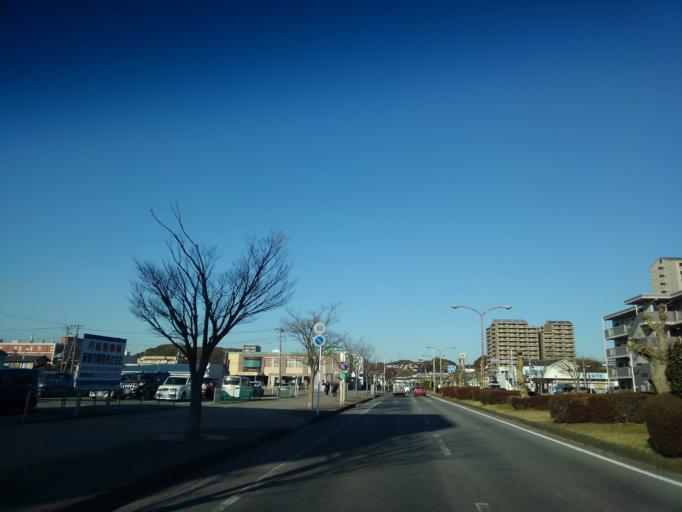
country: JP
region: Chiba
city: Kimitsu
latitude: 35.3314
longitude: 139.8932
